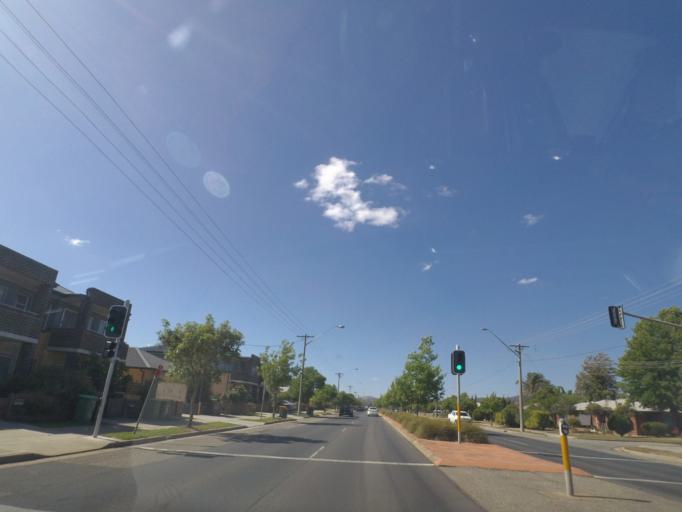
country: AU
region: New South Wales
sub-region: Albury Municipality
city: North Albury
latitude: -36.0607
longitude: 146.9320
